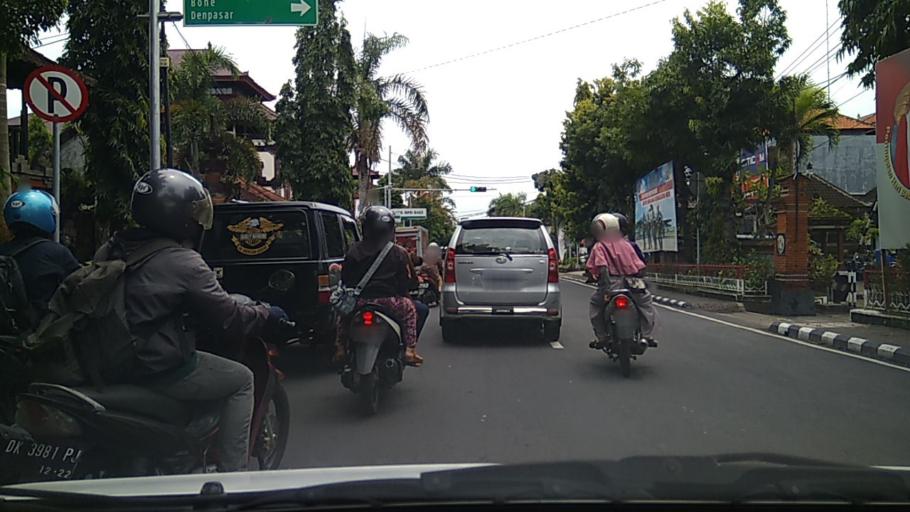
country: ID
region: Bali
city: Banjar Kelodan
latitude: -8.5413
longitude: 115.3245
